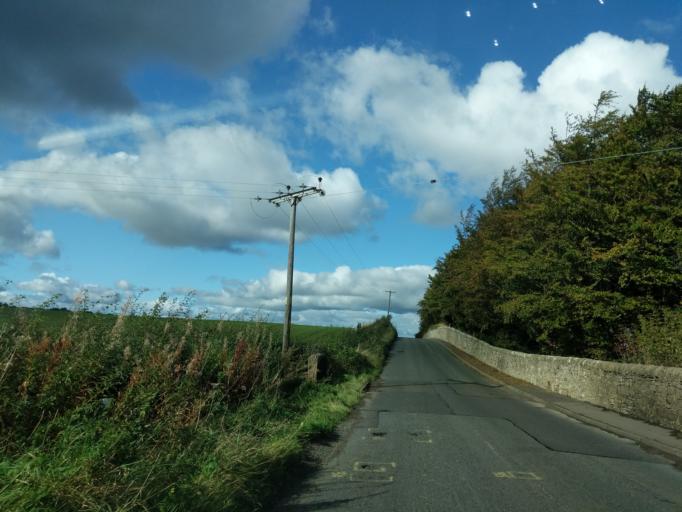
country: GB
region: Scotland
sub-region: Edinburgh
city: Currie
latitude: 55.9063
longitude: -3.3282
